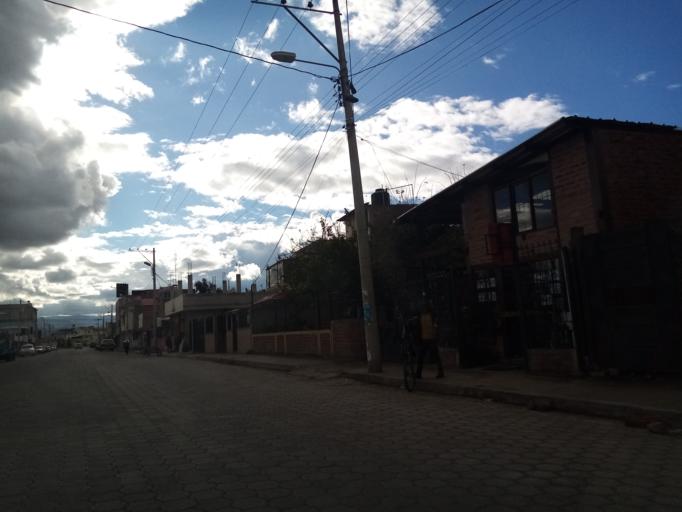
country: EC
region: Chimborazo
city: Riobamba
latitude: -1.6874
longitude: -78.6284
